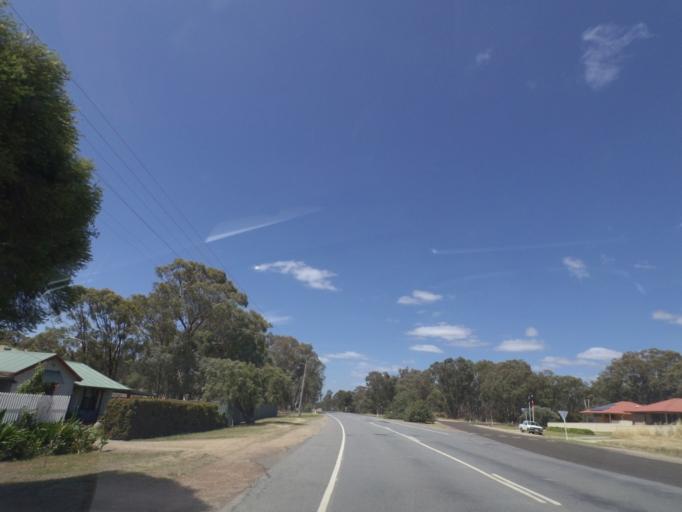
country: AU
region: Victoria
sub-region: Wangaratta
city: Wangaratta
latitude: -36.4633
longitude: 146.2265
